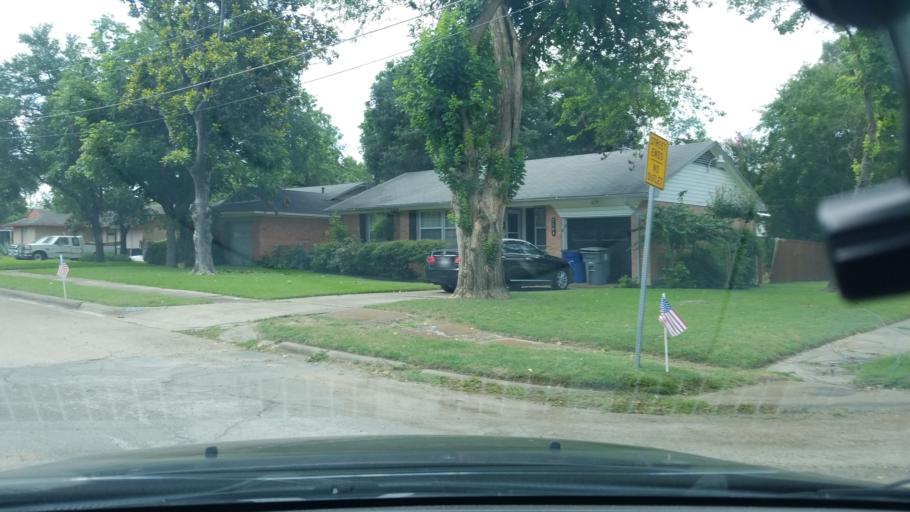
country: US
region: Texas
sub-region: Dallas County
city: Garland
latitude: 32.8293
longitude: -96.6833
